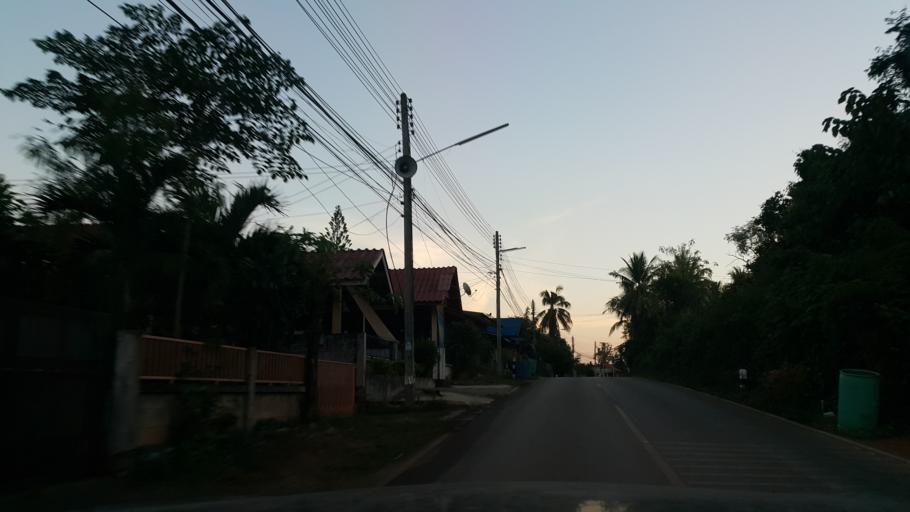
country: TH
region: Uttaradit
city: Uttaradit
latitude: 17.6600
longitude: 100.0933
